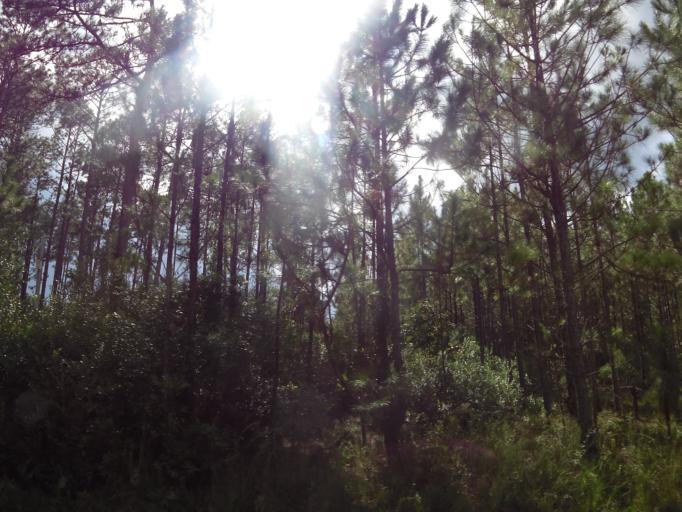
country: US
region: Florida
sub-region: Nassau County
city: Hilliard
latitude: 30.6104
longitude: -82.0781
